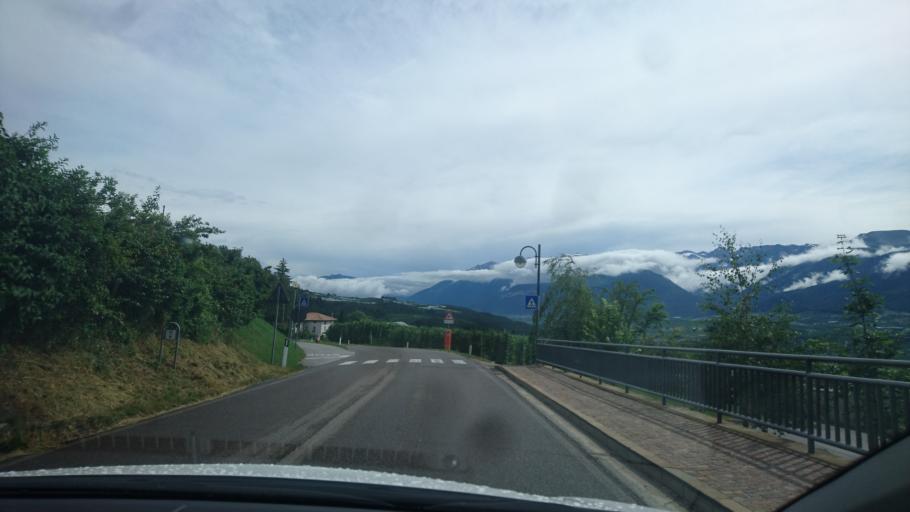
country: IT
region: Trentino-Alto Adige
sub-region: Provincia di Trento
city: Sanzeno
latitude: 46.3777
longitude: 11.0884
